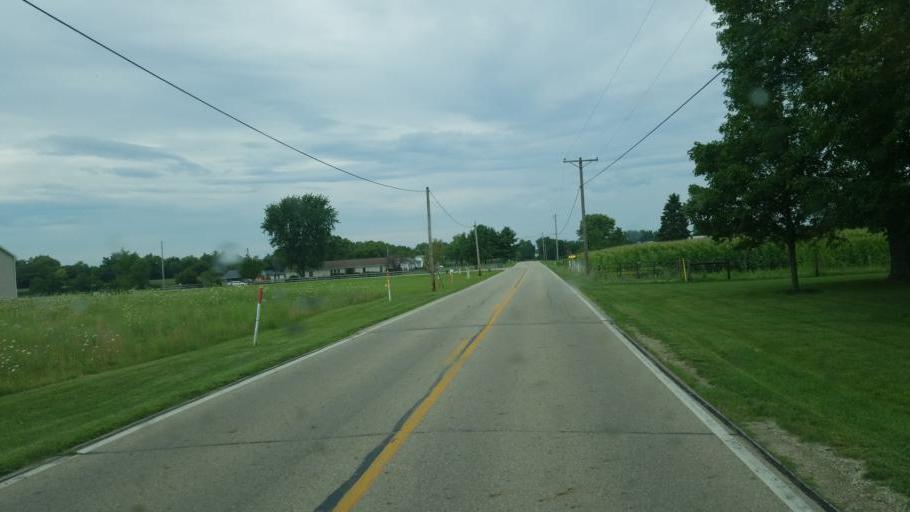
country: US
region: Ohio
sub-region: Pickaway County
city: Ashville
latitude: 39.6971
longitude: -82.9217
